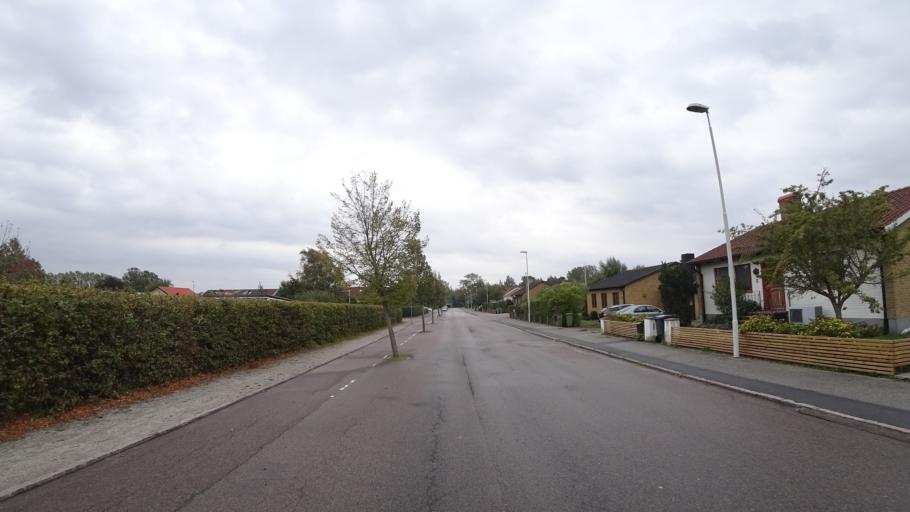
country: SE
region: Skane
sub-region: Kavlinge Kommun
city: Kaevlinge
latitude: 55.7940
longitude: 13.1226
